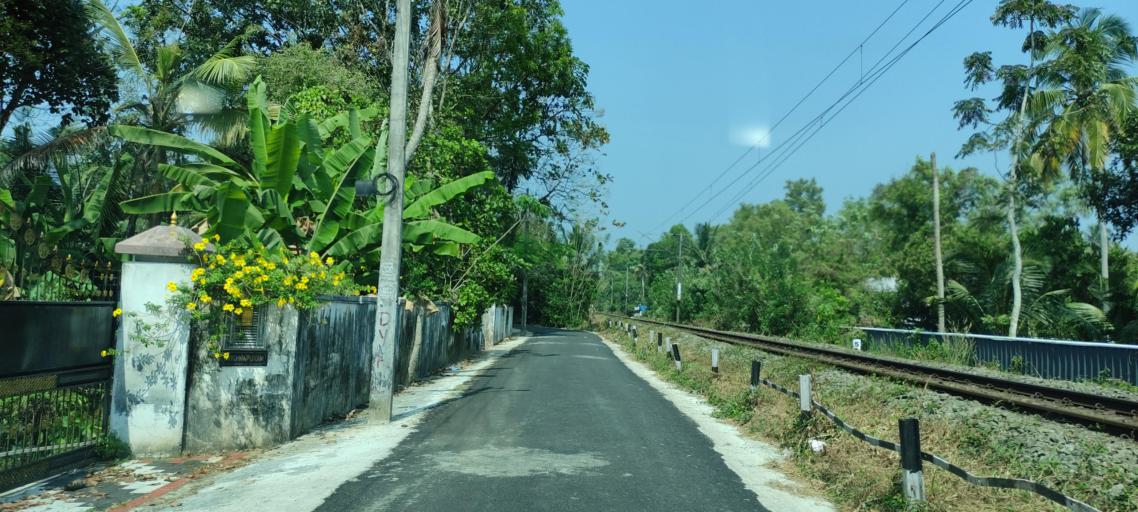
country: IN
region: Kerala
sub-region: Alappuzha
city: Alleppey
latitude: 9.5399
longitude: 76.3209
